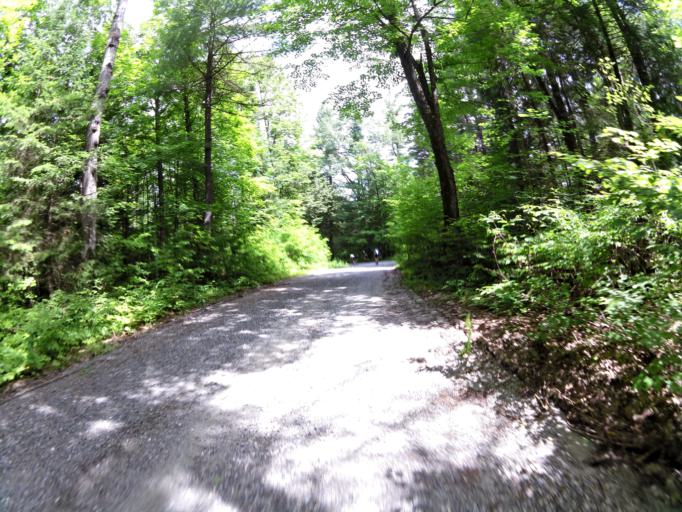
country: CA
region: Ontario
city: Perth
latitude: 45.0245
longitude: -76.5576
